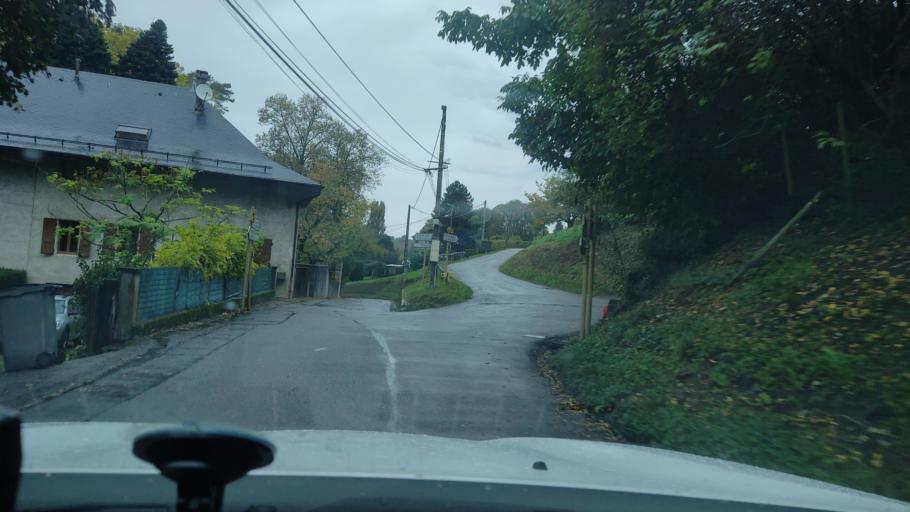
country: FR
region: Rhone-Alpes
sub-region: Departement de la Savoie
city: Cruet
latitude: 45.4963
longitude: 6.1087
